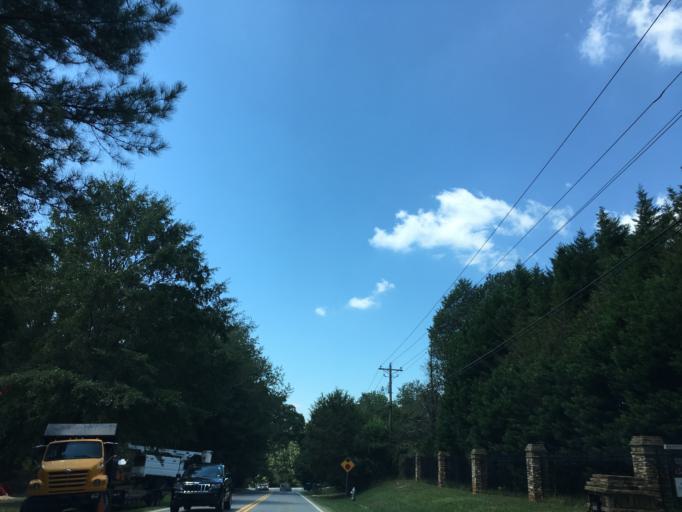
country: US
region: Georgia
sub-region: Fulton County
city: Milton
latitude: 34.1153
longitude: -84.3124
